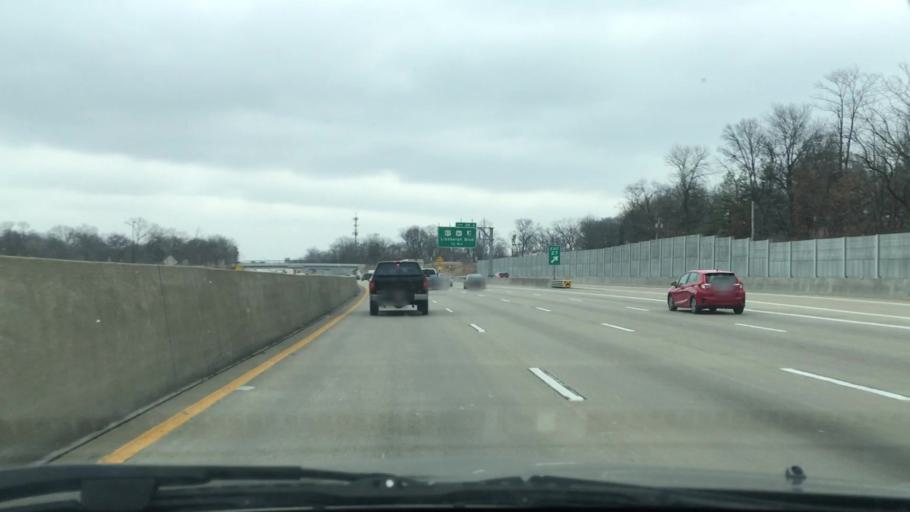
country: US
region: Missouri
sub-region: Saint Louis County
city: Frontenac
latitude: 38.6358
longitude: -90.4205
